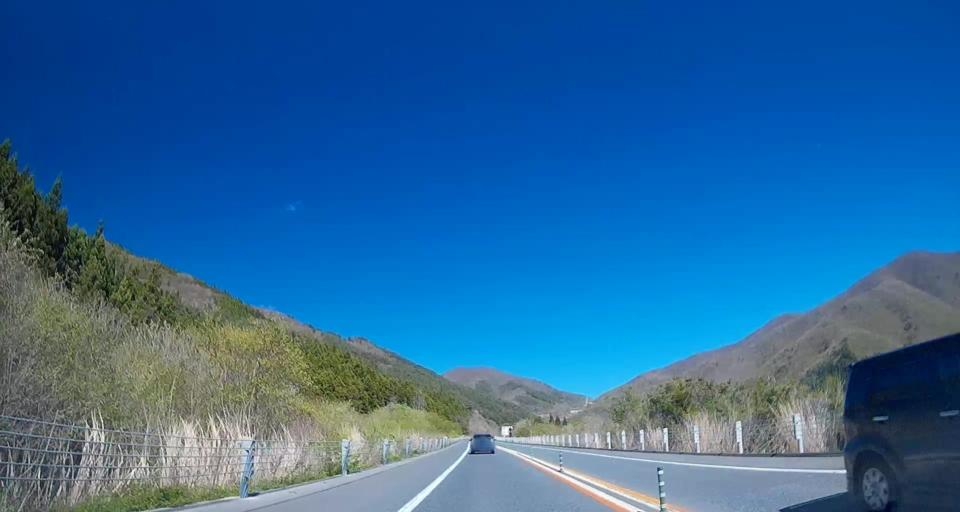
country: JP
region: Iwate
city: Ofunato
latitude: 39.1257
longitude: 141.7490
